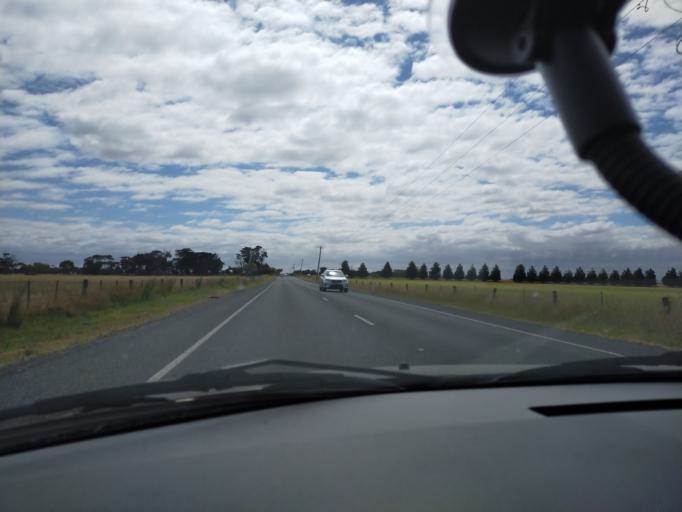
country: AU
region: Victoria
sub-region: Greater Geelong
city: Breakwater
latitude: -38.2549
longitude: 144.3864
